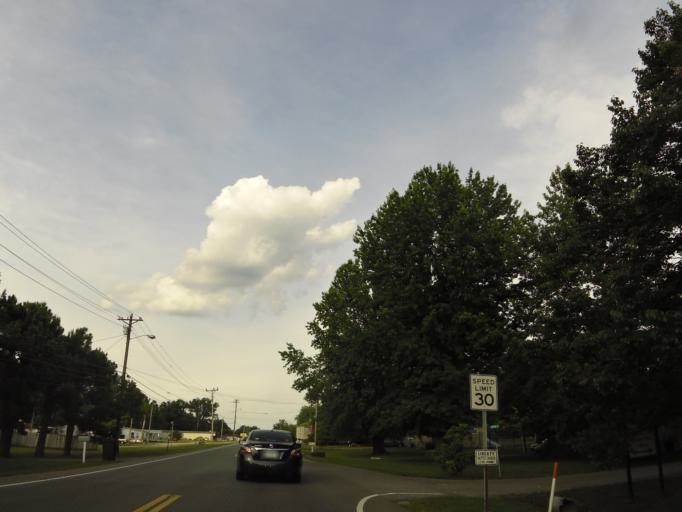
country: US
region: Tennessee
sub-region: Humphreys County
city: McEwen
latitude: 36.1061
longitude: -87.6451
